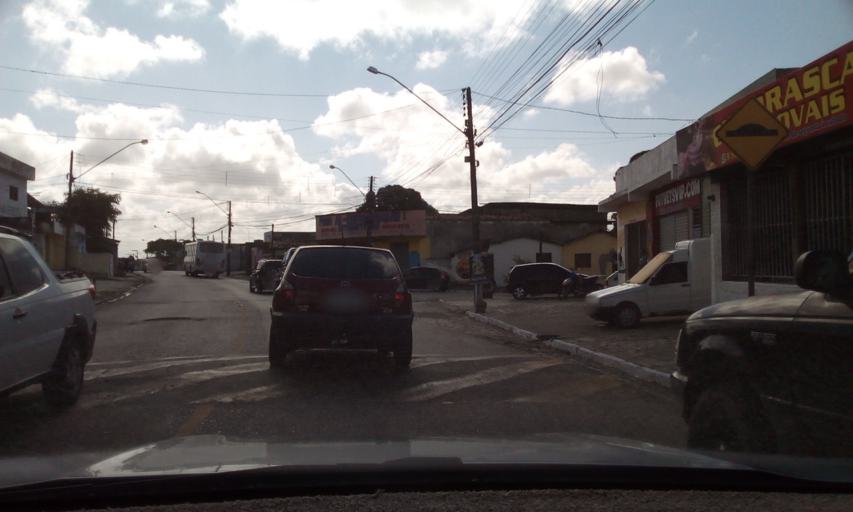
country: BR
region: Paraiba
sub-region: Bayeux
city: Bayeux
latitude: -7.1540
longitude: -34.8971
